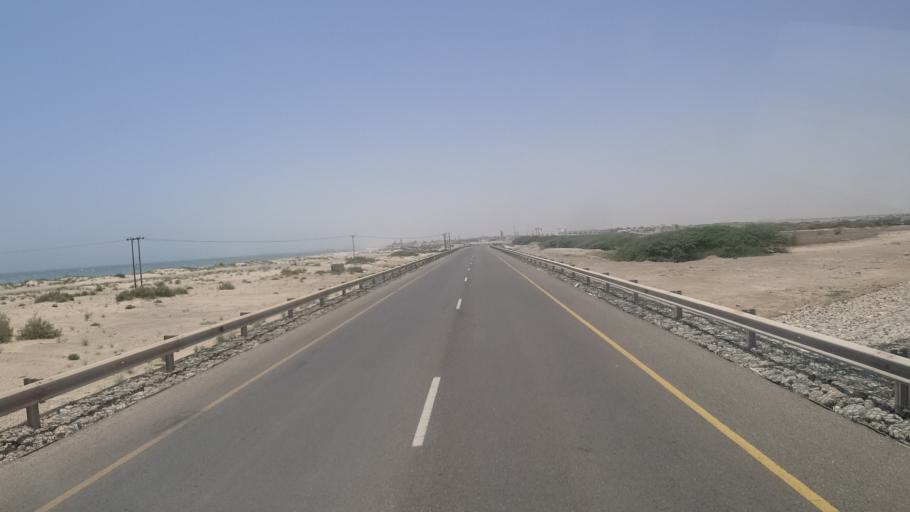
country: OM
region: Ash Sharqiyah
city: Sur
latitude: 22.0928
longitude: 59.6939
